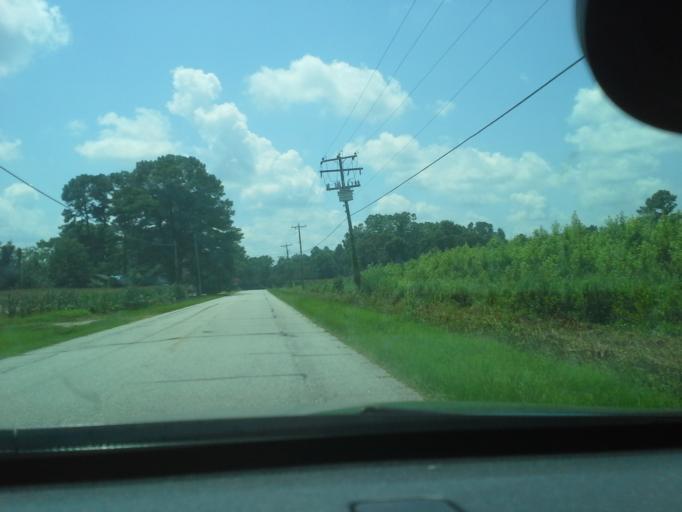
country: US
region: North Carolina
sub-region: Washington County
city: Plymouth
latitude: 35.8416
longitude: -76.7623
